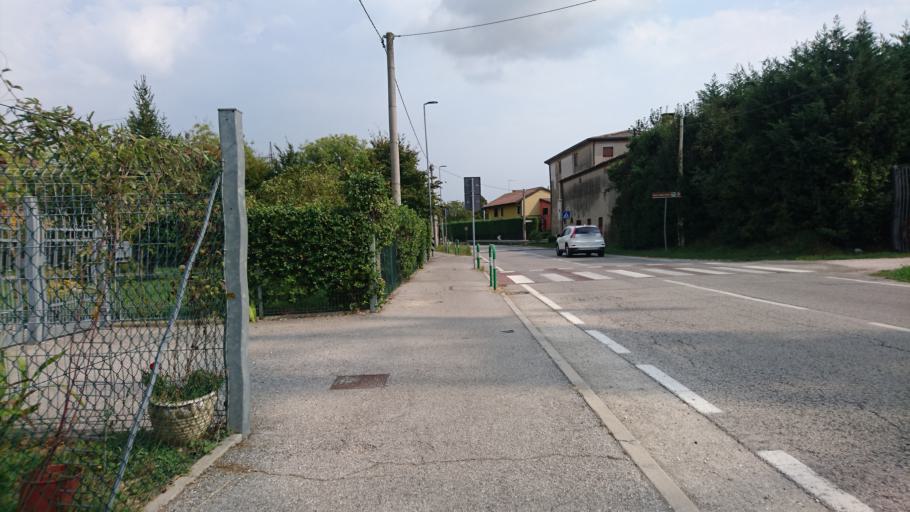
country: IT
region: Veneto
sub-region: Provincia di Padova
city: Villaguattera
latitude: 45.4396
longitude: 11.8471
